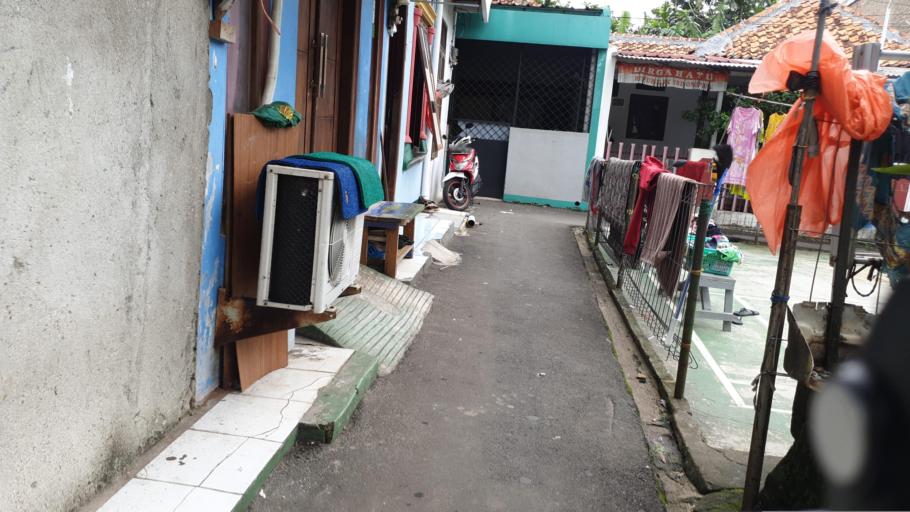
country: ID
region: Jakarta Raya
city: Jakarta
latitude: -6.2496
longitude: 106.7822
